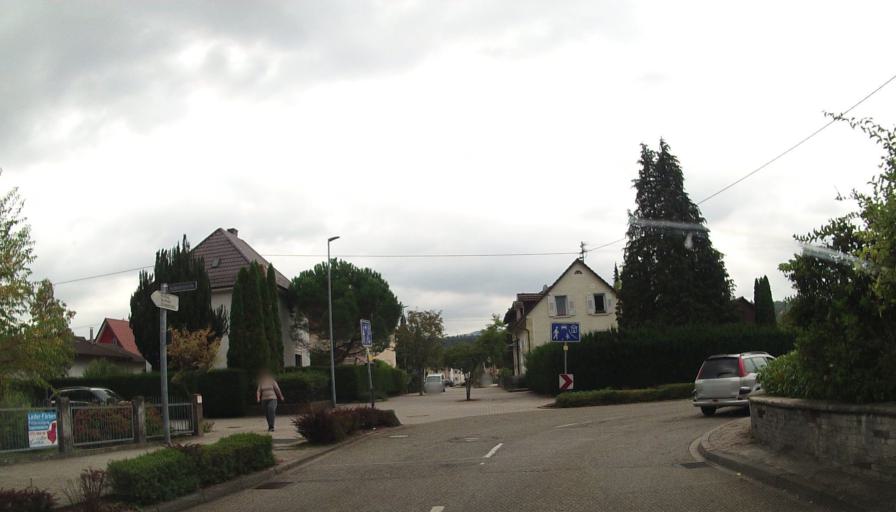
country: DE
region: Baden-Wuerttemberg
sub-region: Karlsruhe Region
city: Gaggenau
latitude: 48.8110
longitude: 8.3156
